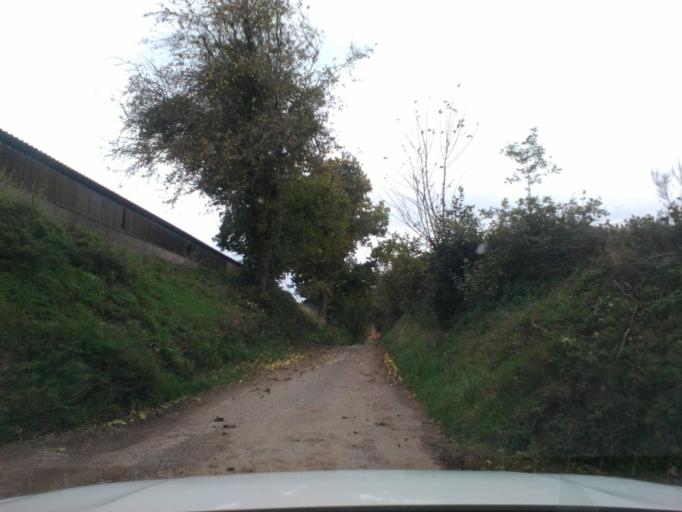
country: FR
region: Lorraine
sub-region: Departement des Vosges
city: Sainte-Marguerite
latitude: 48.3293
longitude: 7.0130
